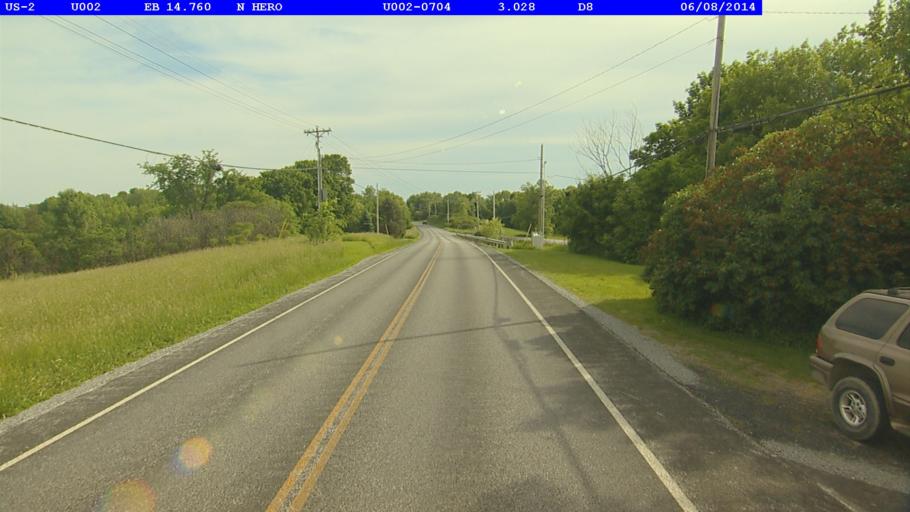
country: US
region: Vermont
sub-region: Grand Isle County
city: North Hero
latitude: 44.8479
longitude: -73.2650
